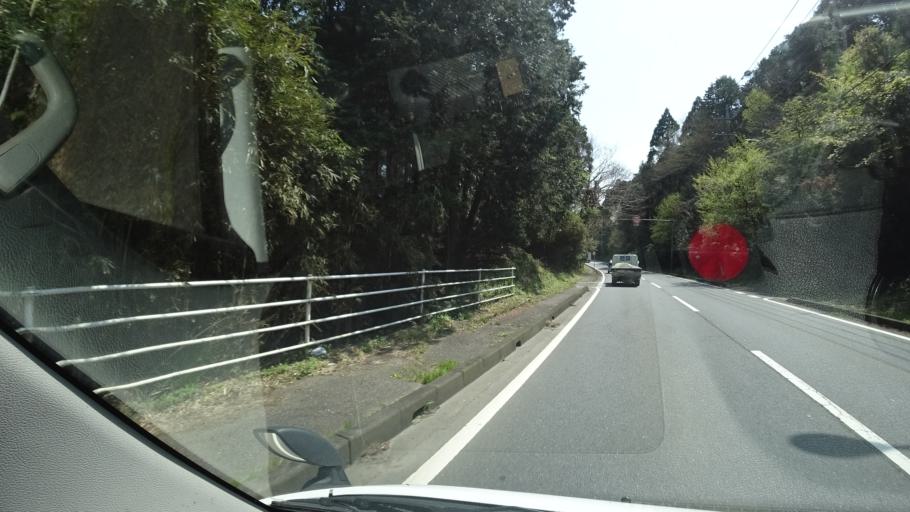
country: JP
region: Chiba
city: Naruto
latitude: 35.6470
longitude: 140.4496
